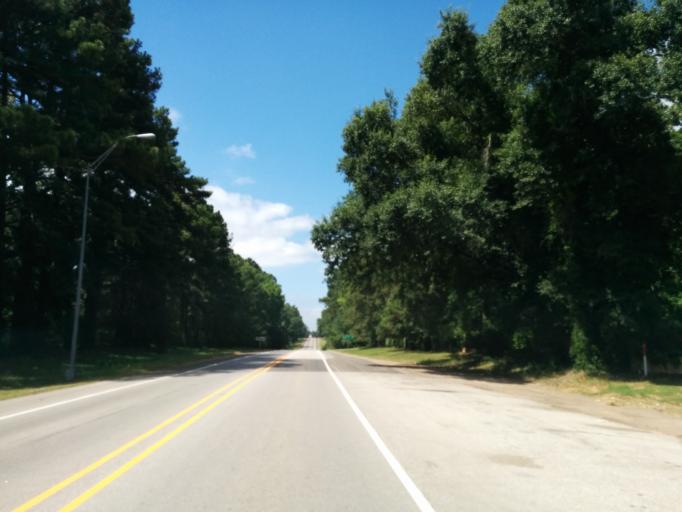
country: US
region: Texas
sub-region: Houston County
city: Crockett
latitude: 31.3088
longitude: -95.4842
